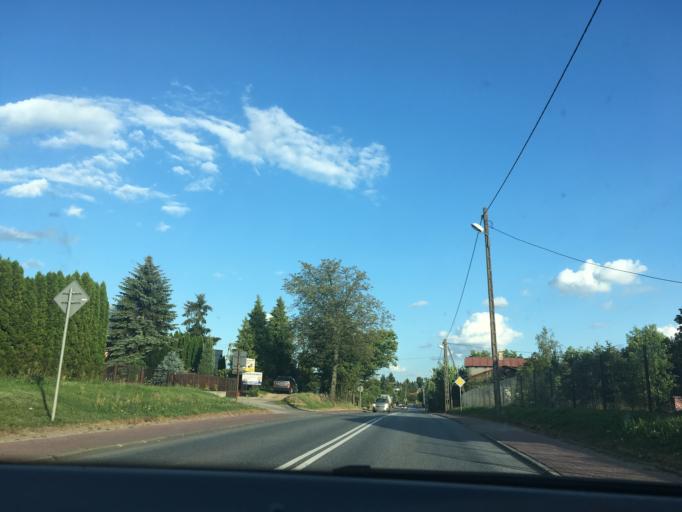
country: PL
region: Masovian Voivodeship
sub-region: Powiat losicki
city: Sarnaki
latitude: 52.3183
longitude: 22.8855
